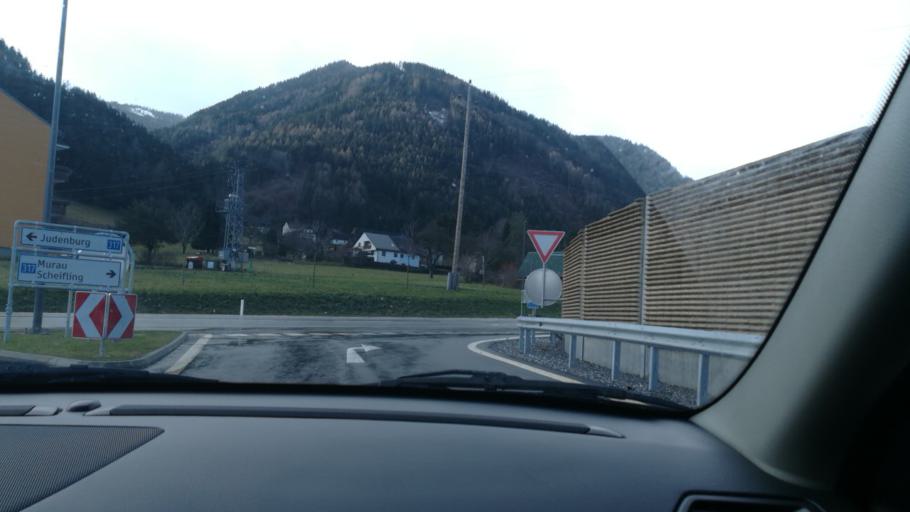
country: AT
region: Styria
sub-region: Politischer Bezirk Murtal
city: Sankt Georgen ob Judenburg
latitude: 47.2057
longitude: 14.5009
